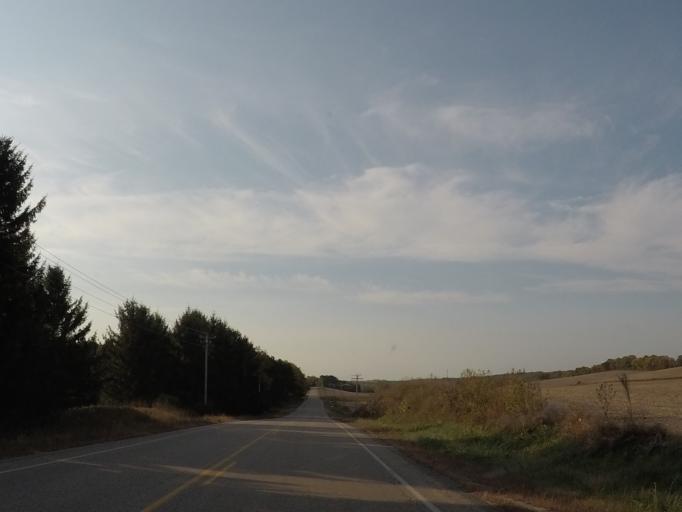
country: US
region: Wisconsin
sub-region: Dane County
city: Cross Plains
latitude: 43.0401
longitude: -89.6163
